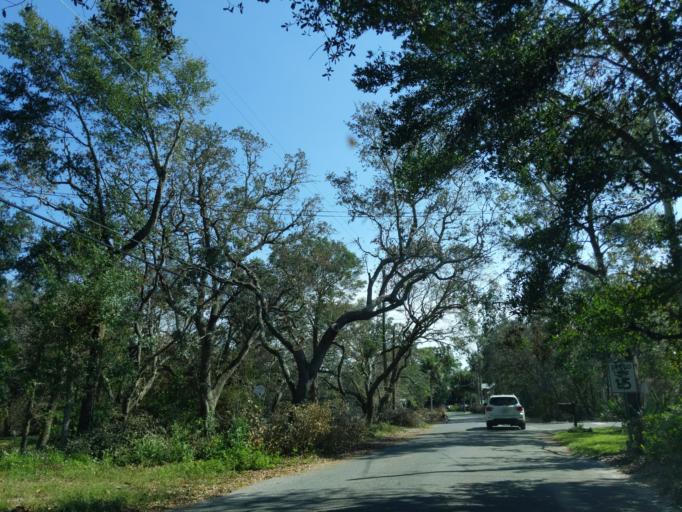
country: US
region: Florida
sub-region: Santa Rosa County
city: Gulf Breeze
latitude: 30.3650
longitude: -87.1830
